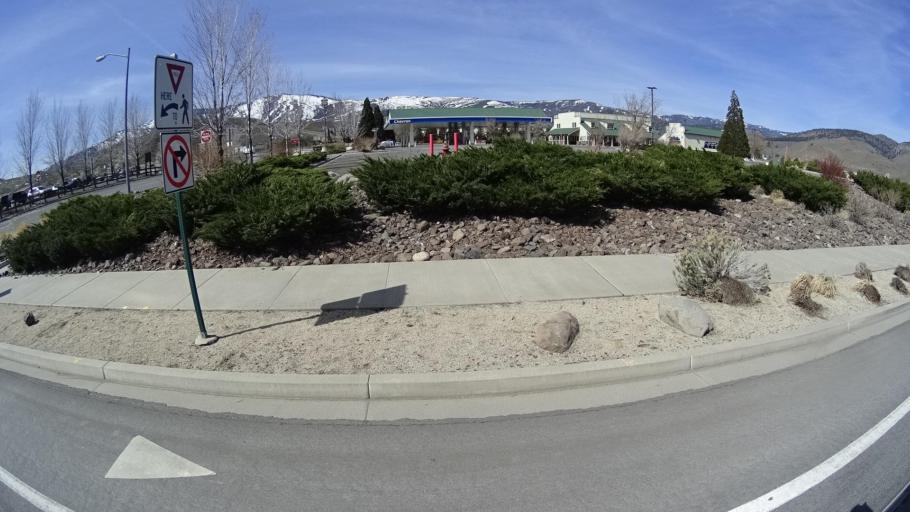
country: US
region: Nevada
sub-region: Washoe County
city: Verdi
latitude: 39.5129
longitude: -119.9646
